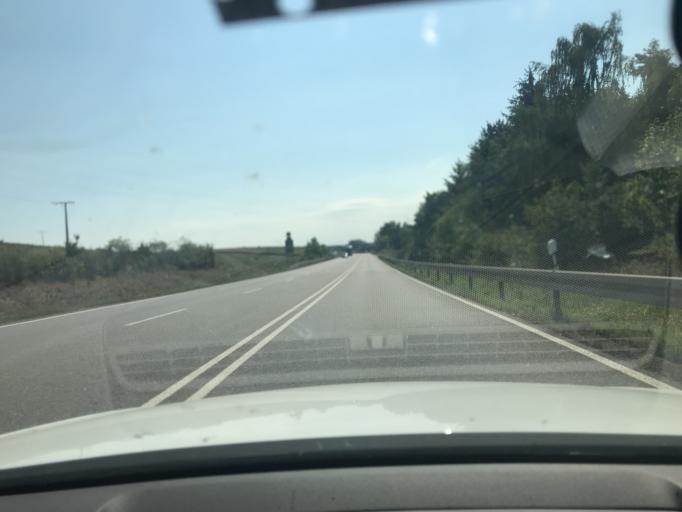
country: DE
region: Bavaria
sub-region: Upper Palatinate
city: Poppenricht
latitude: 49.4555
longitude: 11.8194
